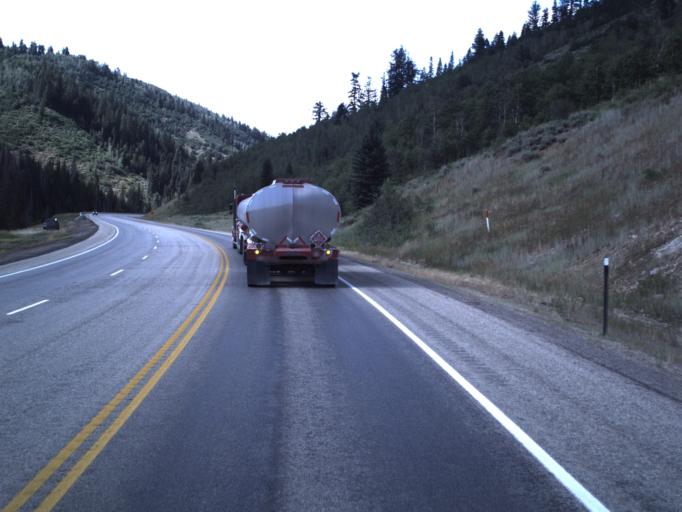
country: US
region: Utah
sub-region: Wasatch County
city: Heber
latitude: 40.3209
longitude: -111.2590
